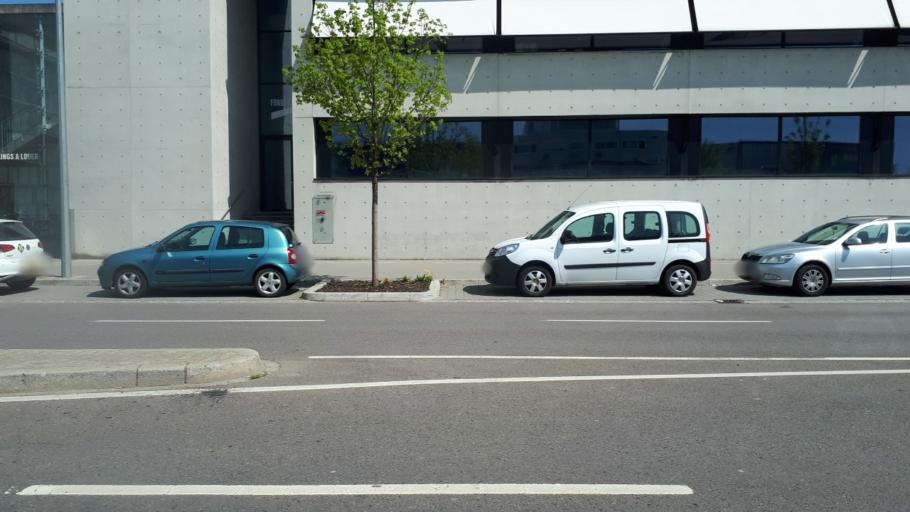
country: LU
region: Luxembourg
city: Kirchberg
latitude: 49.6222
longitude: 6.1513
